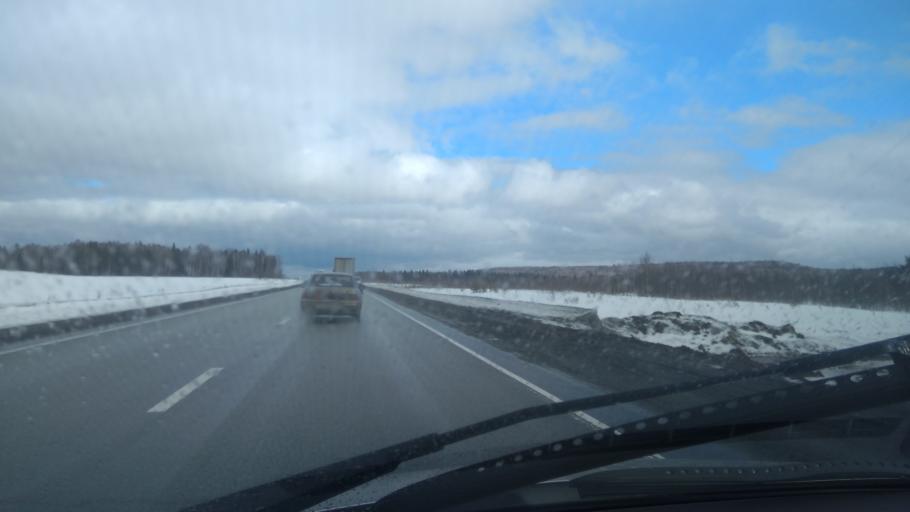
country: RU
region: Sverdlovsk
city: Bisert'
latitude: 56.8103
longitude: 58.7329
